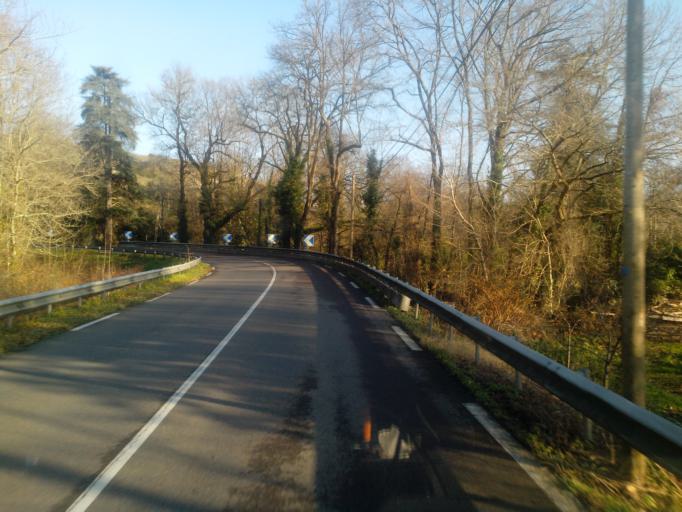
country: FR
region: Midi-Pyrenees
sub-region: Departement du Lot
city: Vayrac
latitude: 44.9080
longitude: 1.6375
